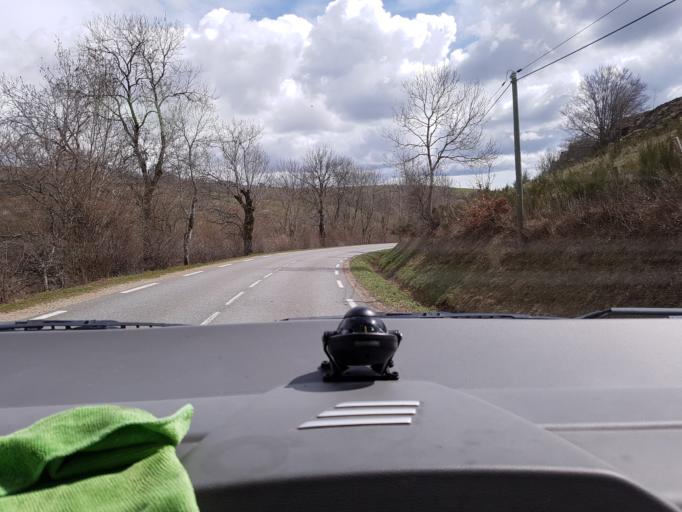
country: FR
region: Midi-Pyrenees
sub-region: Departement de l'Aveyron
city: Laguiole
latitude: 44.7025
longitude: 2.8628
